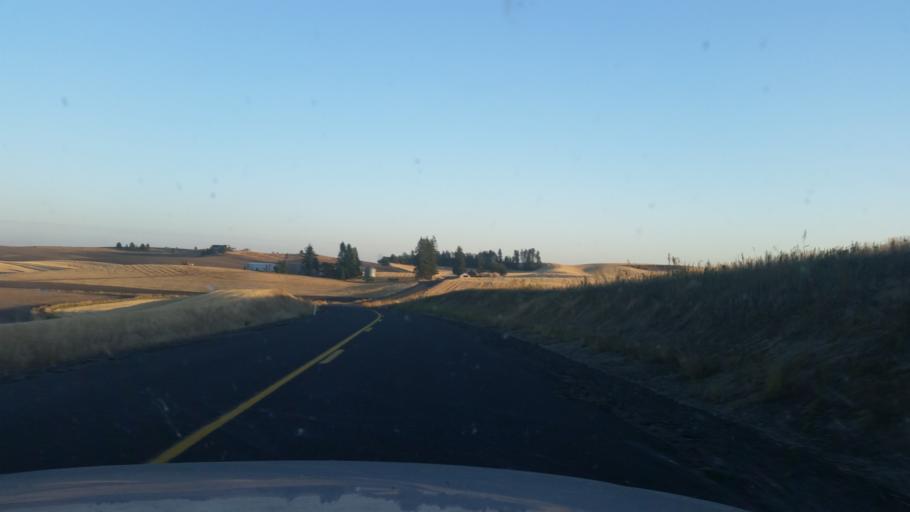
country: US
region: Washington
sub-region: Spokane County
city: Cheney
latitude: 47.5265
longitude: -117.6021
